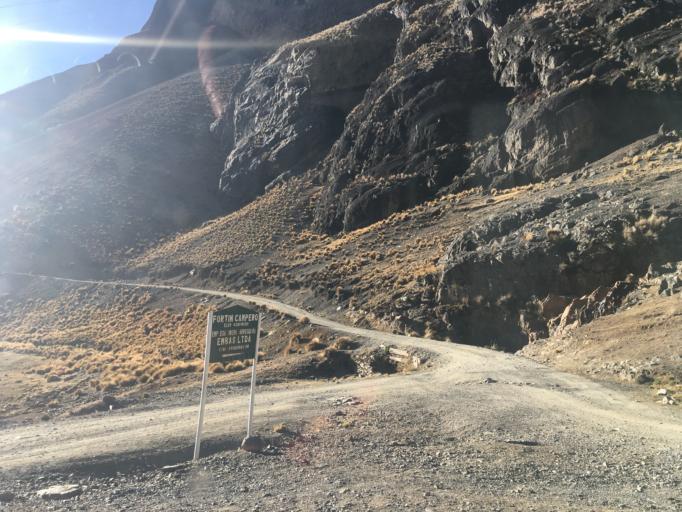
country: BO
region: La Paz
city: Quime
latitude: -17.0482
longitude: -67.2950
